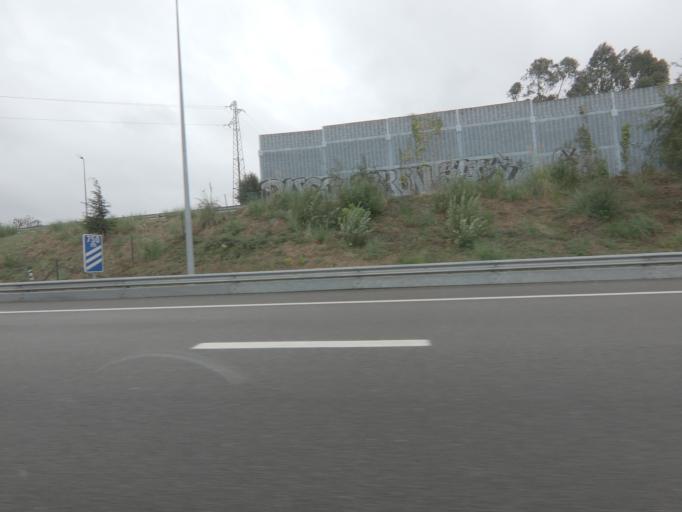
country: PT
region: Porto
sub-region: Matosinhos
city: Sao Mamede de Infesta
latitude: 41.1992
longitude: -8.6036
